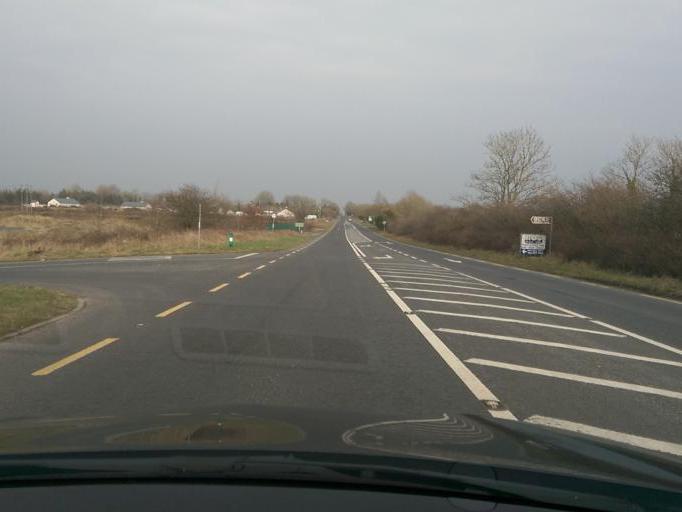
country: IE
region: Connaught
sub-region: Roscommon
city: Roscommon
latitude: 53.6394
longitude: -8.1614
